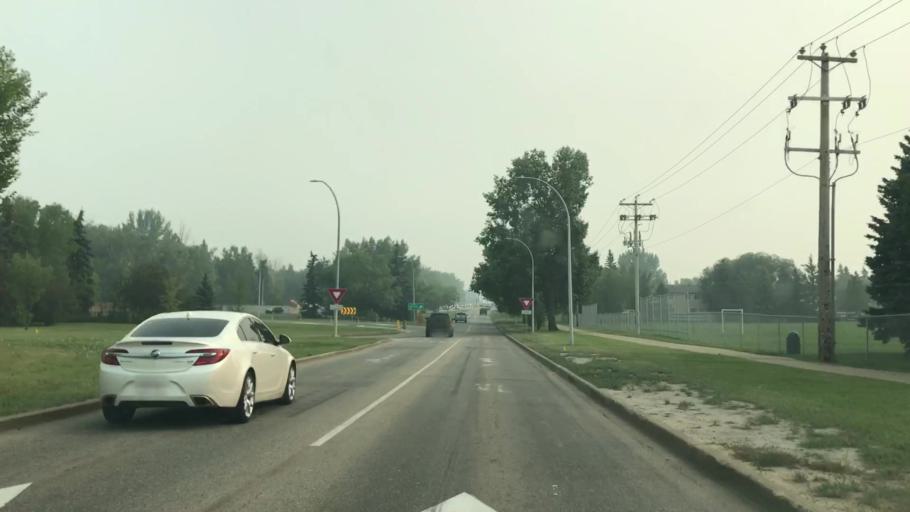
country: CA
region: Alberta
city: Sherwood Park
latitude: 53.5196
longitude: -113.3201
